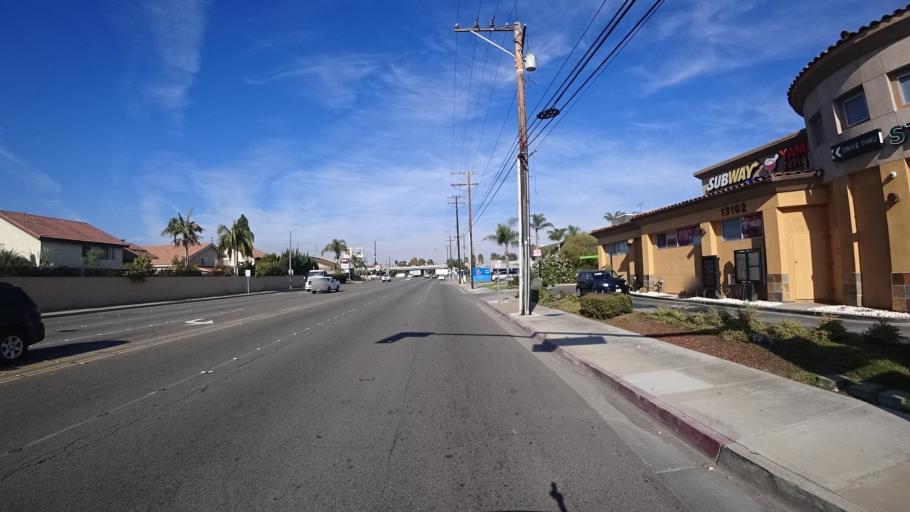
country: US
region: California
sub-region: Orange County
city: Westminster
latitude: 33.7720
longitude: -118.0073
